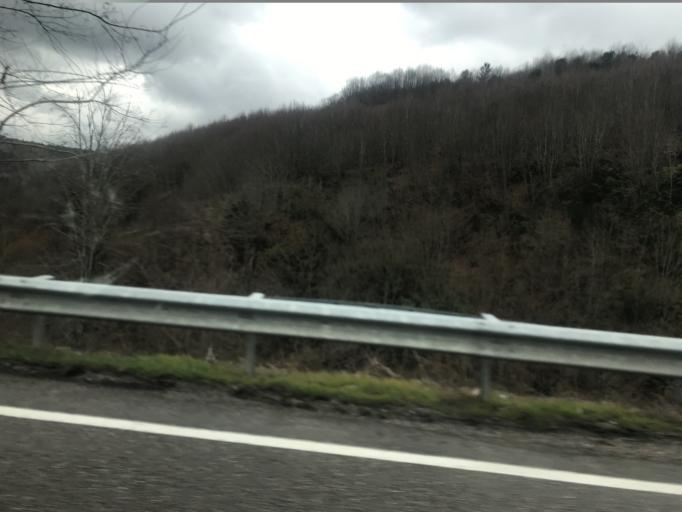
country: TR
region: Bartin
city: Amasra
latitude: 41.6989
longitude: 32.3842
